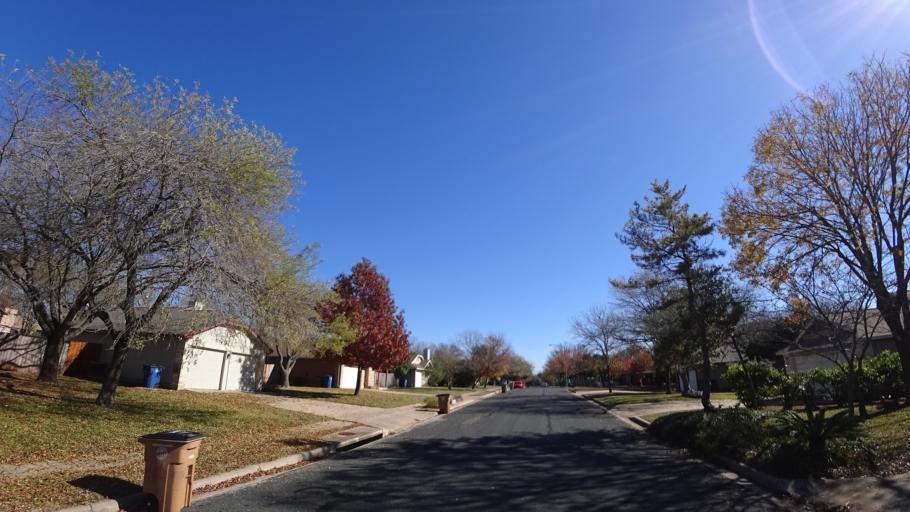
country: US
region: Texas
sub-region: Travis County
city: Wells Branch
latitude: 30.4161
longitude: -97.7013
